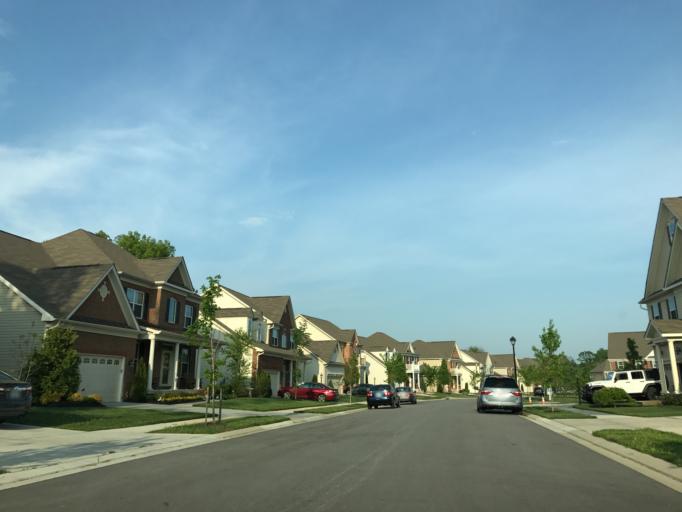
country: US
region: Maryland
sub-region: Baltimore County
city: White Marsh
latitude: 39.3712
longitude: -76.4164
